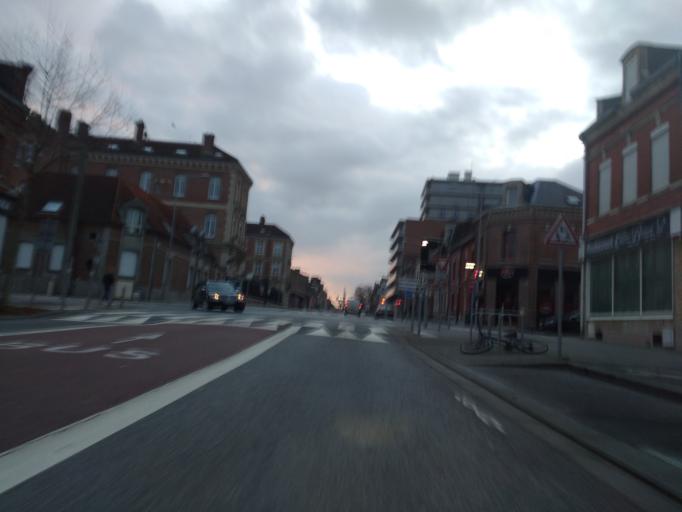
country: FR
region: Picardie
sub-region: Departement de la Somme
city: Rivery
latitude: 49.8855
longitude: 2.3197
